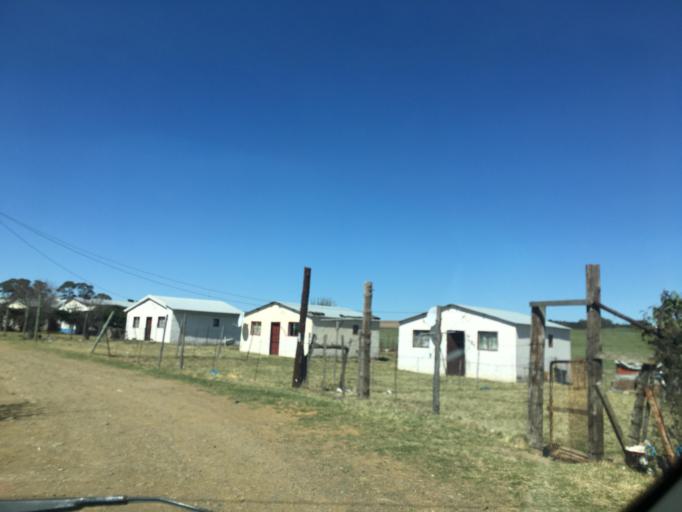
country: ZA
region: Eastern Cape
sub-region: Chris Hani District Municipality
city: Elliot
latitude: -31.3387
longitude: 27.8333
